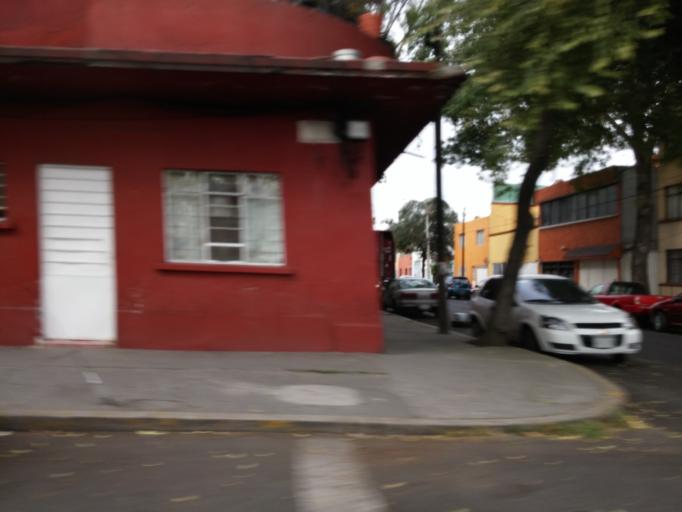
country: MX
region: Mexico City
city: Azcapotzalco
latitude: 19.4616
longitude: -99.1753
